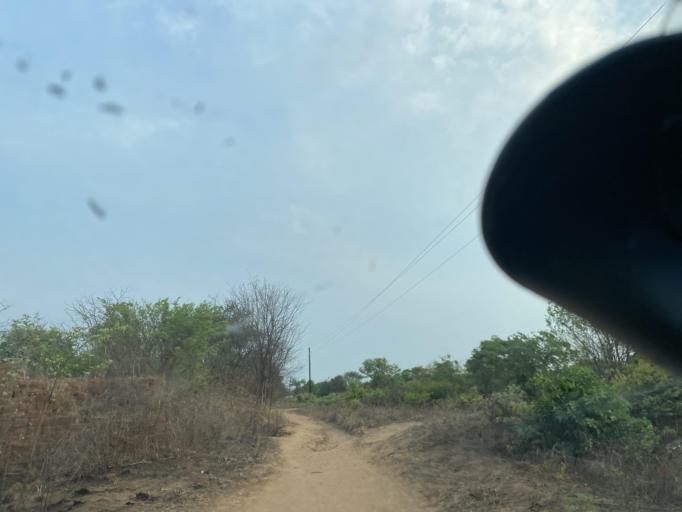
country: ZM
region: Lusaka
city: Chongwe
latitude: -15.2065
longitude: 28.4995
